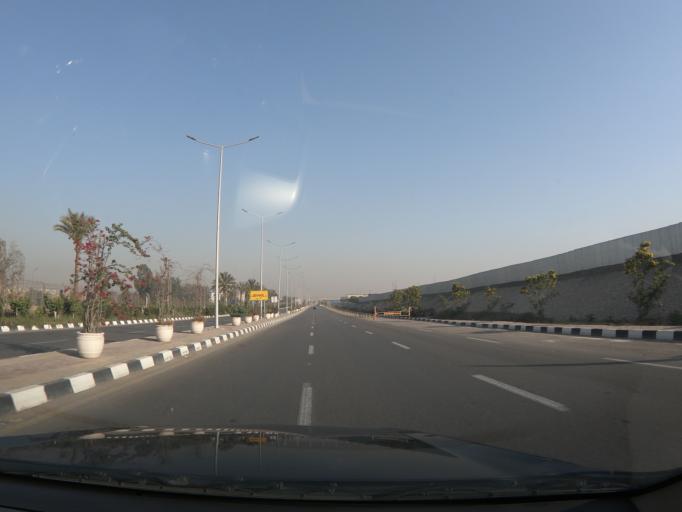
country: EG
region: Muhafazat al Qalyubiyah
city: Al Khankah
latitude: 30.1051
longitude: 31.3874
